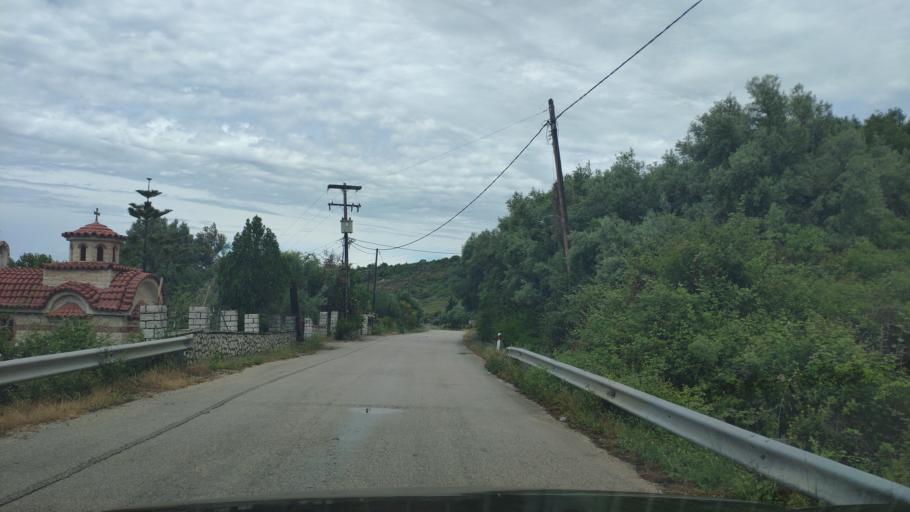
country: GR
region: West Greece
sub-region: Nomos Aitolias kai Akarnanias
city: Palairos
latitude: 38.7550
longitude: 20.8863
